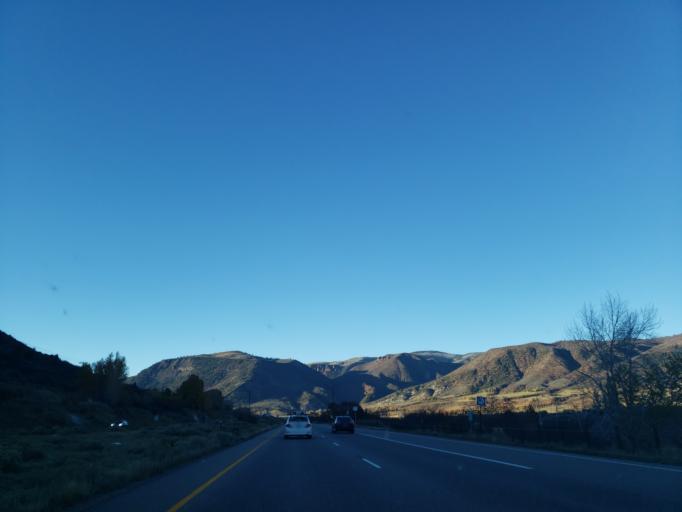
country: US
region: Colorado
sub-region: Pitkin County
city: Snowmass Village
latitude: 39.2670
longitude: -106.8898
